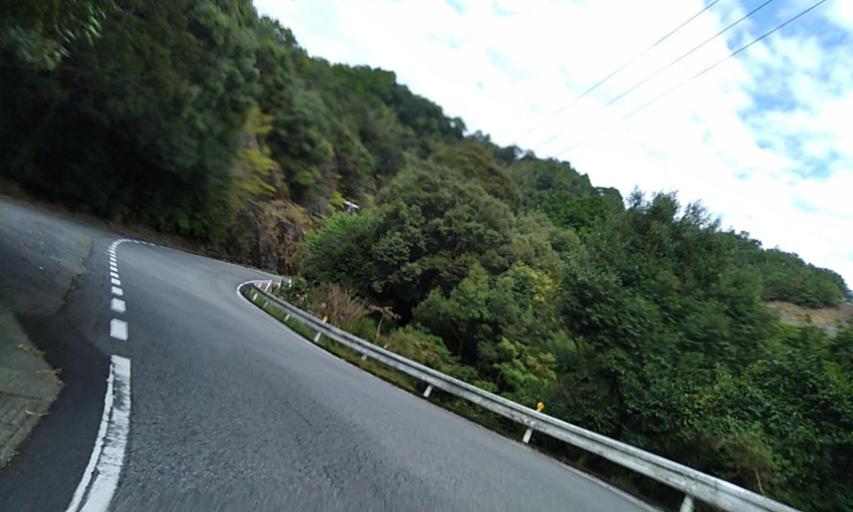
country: JP
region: Wakayama
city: Shingu
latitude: 33.5420
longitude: 135.8319
